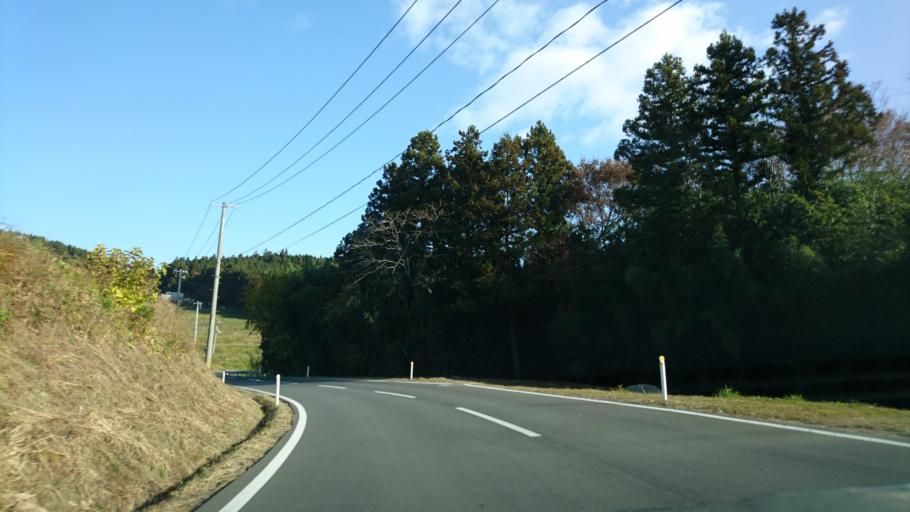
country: JP
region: Iwate
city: Ichinoseki
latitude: 38.8729
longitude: 141.3166
